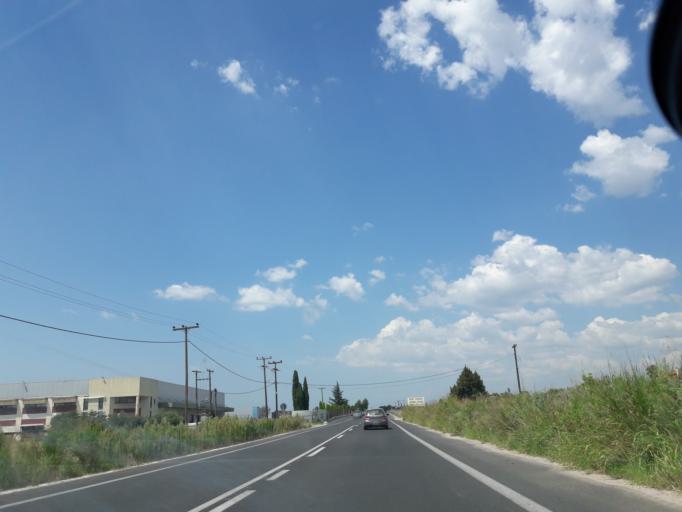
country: GR
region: Central Macedonia
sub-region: Nomos Thessalonikis
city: Agia Paraskevi
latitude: 40.5183
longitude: 23.0639
